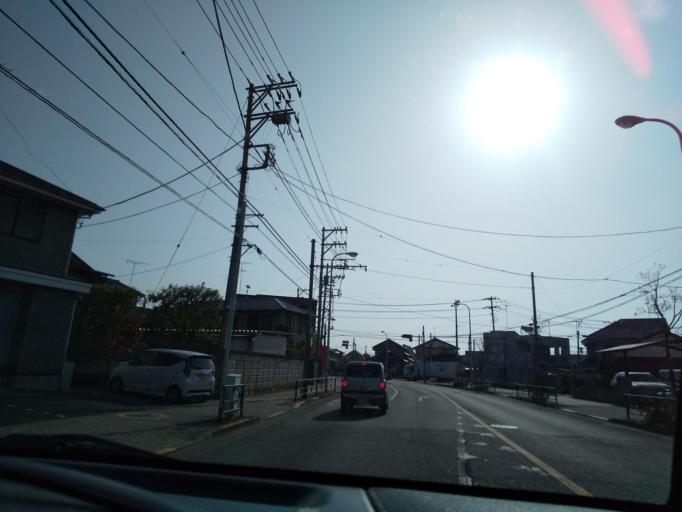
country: JP
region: Tokyo
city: Fussa
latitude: 35.7278
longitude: 139.3174
